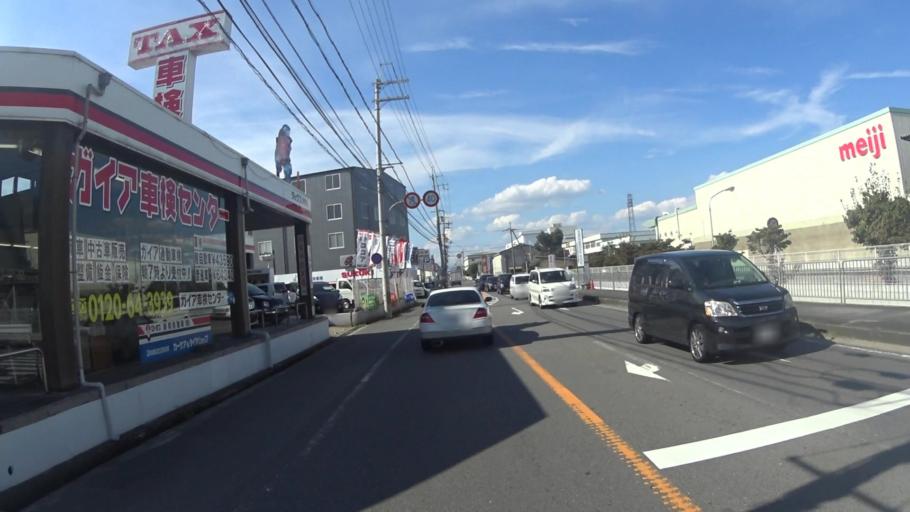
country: JP
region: Kyoto
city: Tanabe
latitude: 34.8401
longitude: 135.7516
